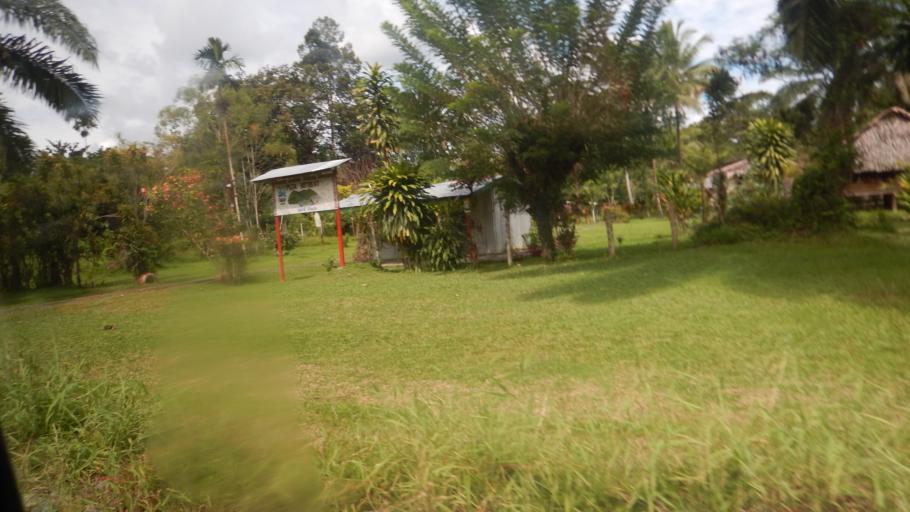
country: PG
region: Northern Province
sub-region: Sohe
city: Kokoda
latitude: -8.9051
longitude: 147.9713
